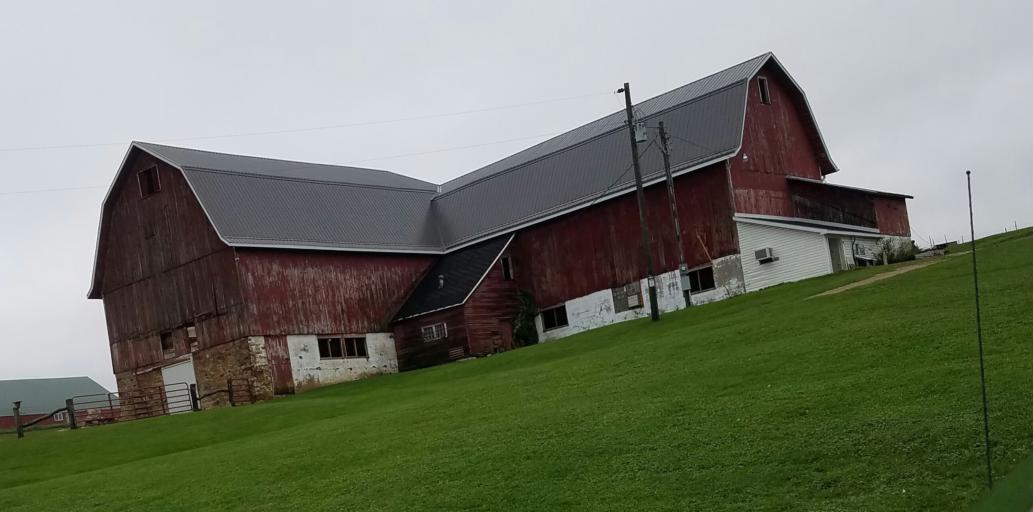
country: US
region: Wisconsin
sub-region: Vernon County
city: Hillsboro
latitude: 43.6188
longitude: -90.2414
